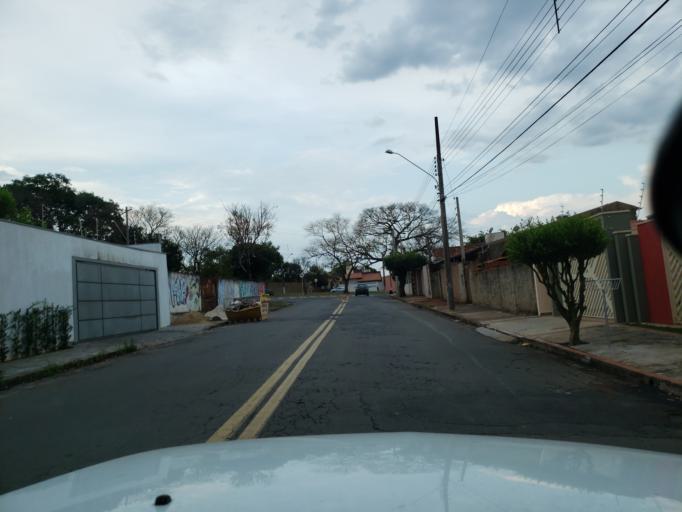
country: BR
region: Sao Paulo
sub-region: Moji-Guacu
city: Mogi-Gaucu
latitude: -22.3620
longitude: -46.9405
